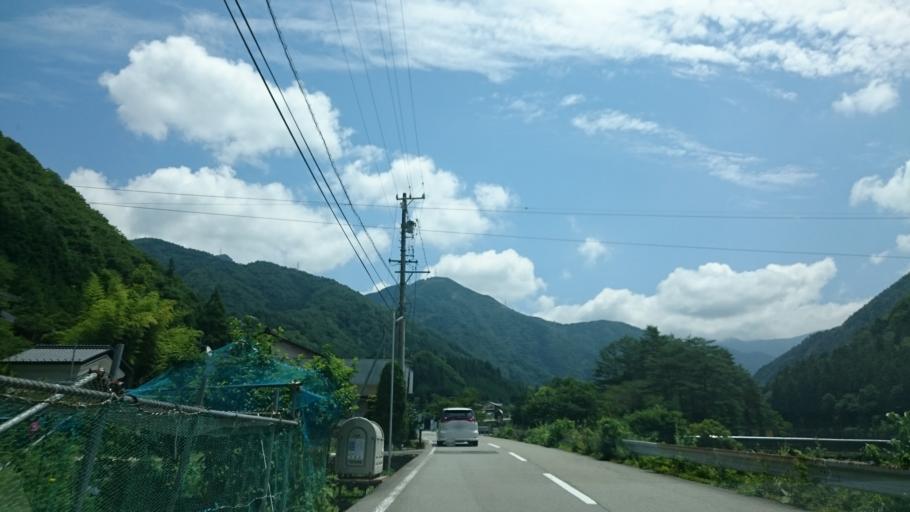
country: JP
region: Gifu
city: Takayama
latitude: 35.9257
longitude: 137.3115
